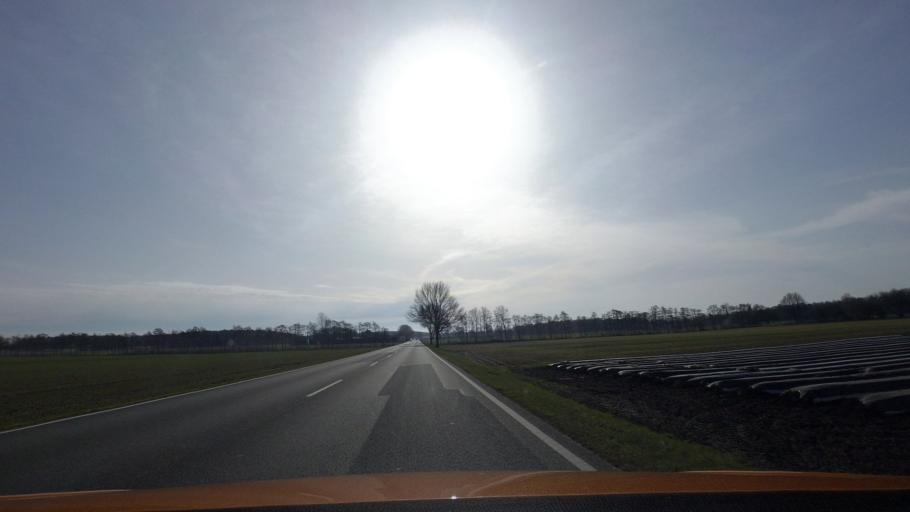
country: DE
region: Lower Saxony
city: Uchte
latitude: 52.5241
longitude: 8.8897
